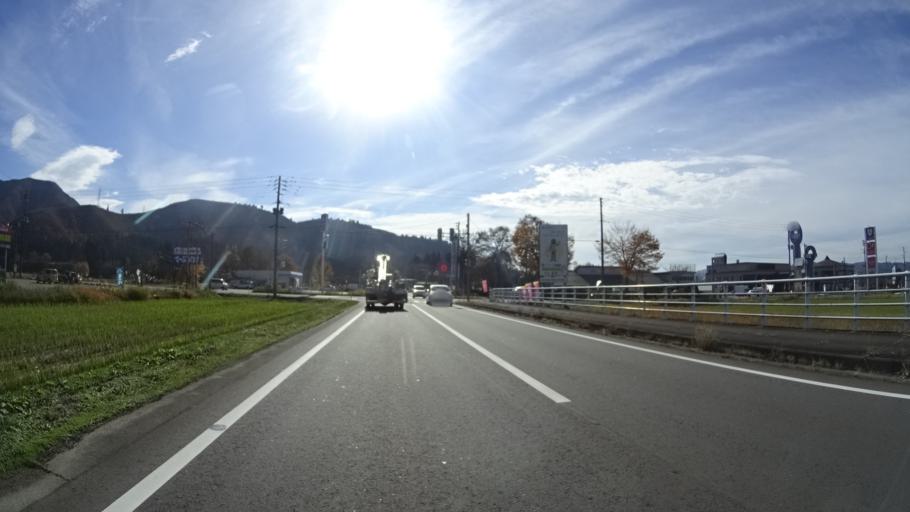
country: JP
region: Niigata
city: Muikamachi
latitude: 37.2250
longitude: 138.9840
